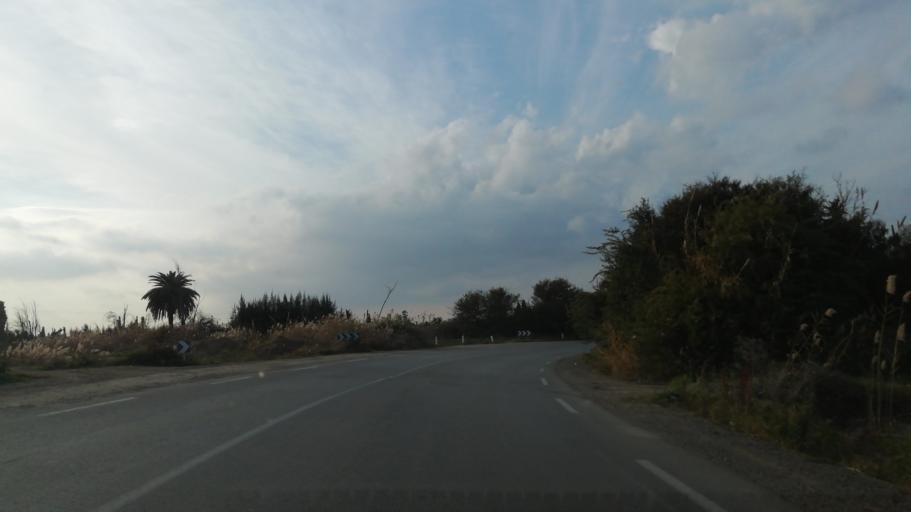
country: DZ
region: Mascara
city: Mascara
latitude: 35.6174
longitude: 0.0489
